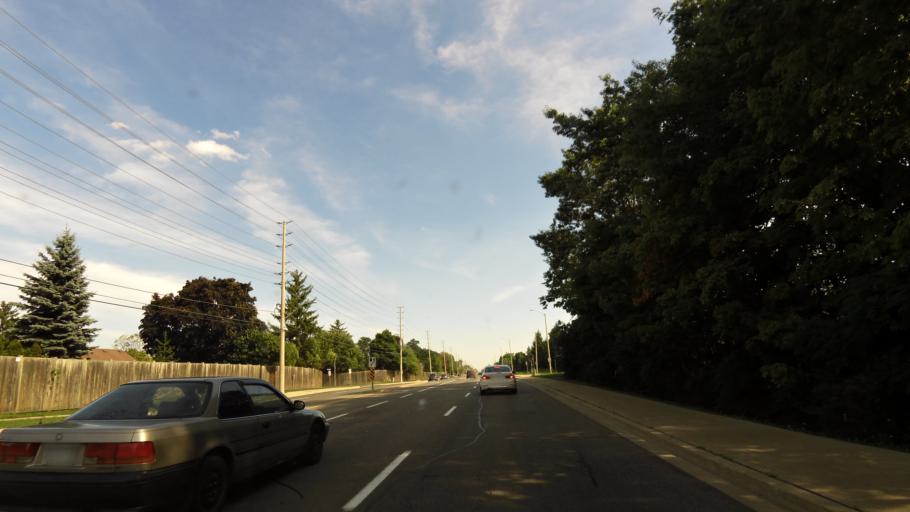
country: CA
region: Ontario
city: Mississauga
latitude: 43.5344
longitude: -79.6975
